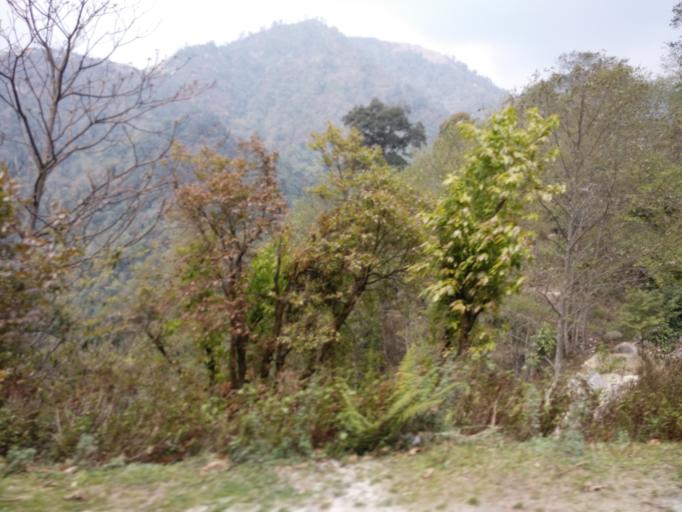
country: NP
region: Central Region
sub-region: Narayani Zone
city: Hitura
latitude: 27.5669
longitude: 85.0726
